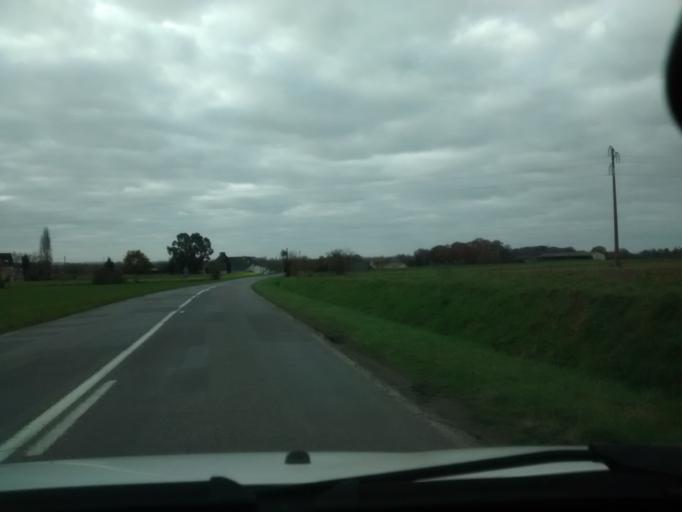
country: FR
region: Brittany
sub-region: Departement d'Ille-et-Vilaine
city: Chavagne
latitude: 48.0658
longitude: -1.7698
